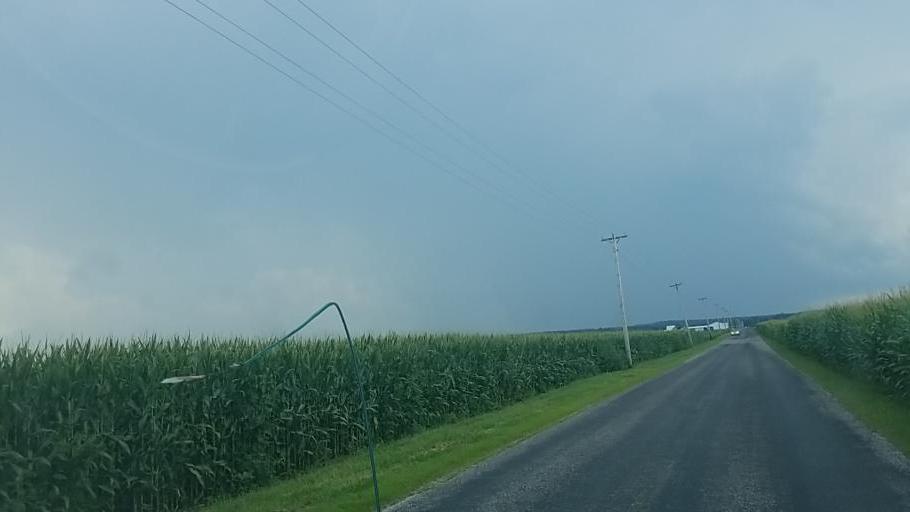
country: US
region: Ohio
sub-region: Medina County
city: Lodi
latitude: 41.0169
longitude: -82.0183
